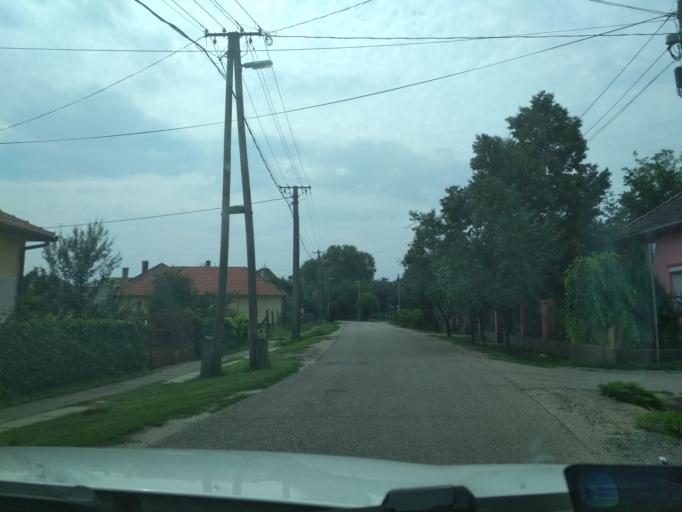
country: HU
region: Jasz-Nagykun-Szolnok
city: Tiszafured
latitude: 47.6228
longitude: 20.7572
